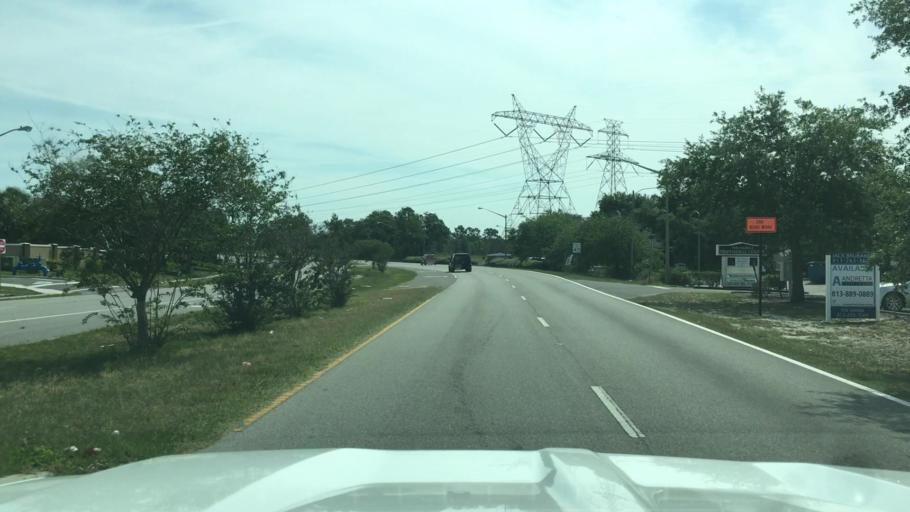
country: US
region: Florida
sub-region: Pasco County
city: Shady Hills
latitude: 28.4372
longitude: -82.5465
